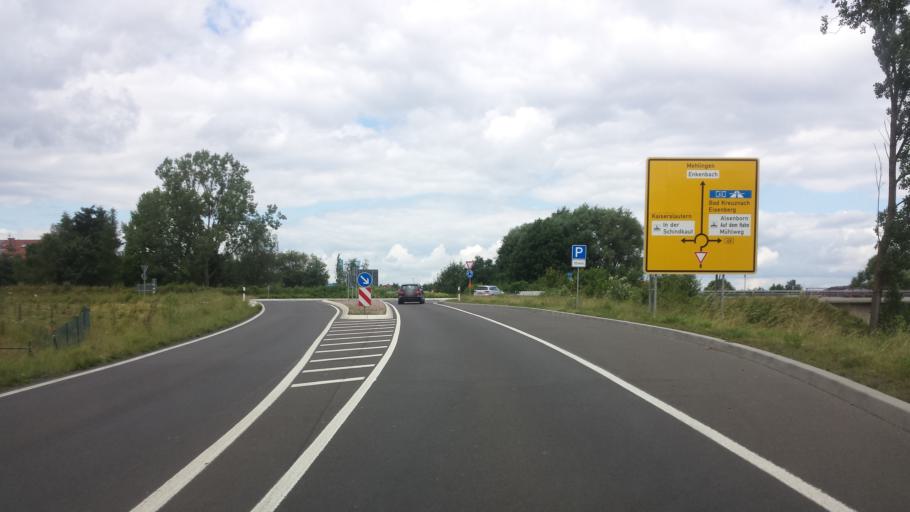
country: DE
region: Rheinland-Pfalz
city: Enkenbach-Alsenborn
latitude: 49.4821
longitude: 7.9025
